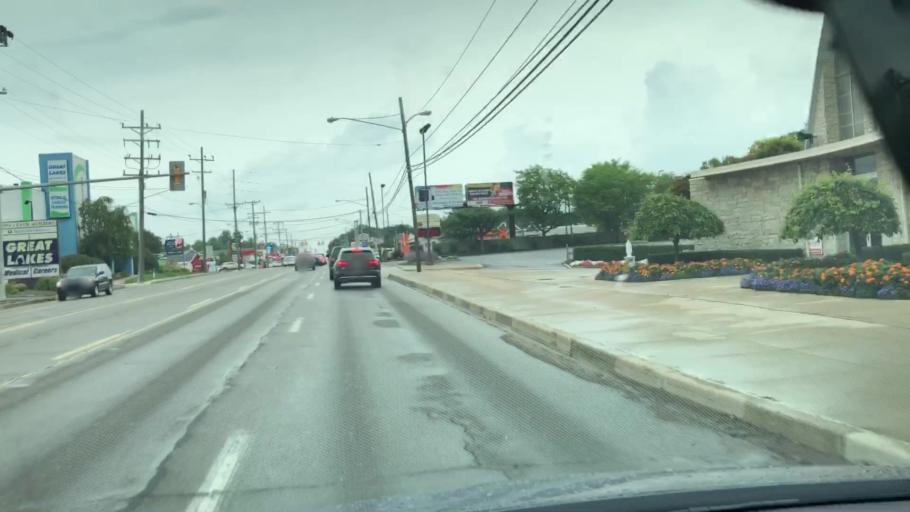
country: US
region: Pennsylvania
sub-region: Erie County
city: Erie
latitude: 42.0785
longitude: -80.0916
